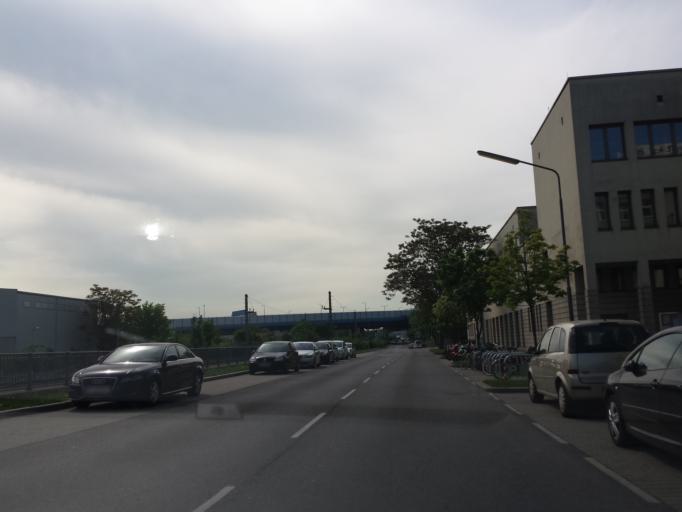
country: AT
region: Vienna
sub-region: Wien Stadt
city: Vienna
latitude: 48.1860
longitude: 16.4016
